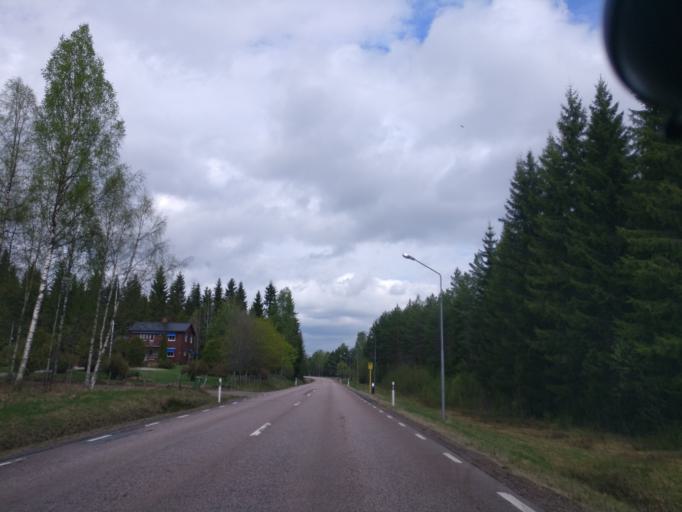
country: SE
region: Vaermland
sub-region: Hagfors Kommun
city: Ekshaerad
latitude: 60.1397
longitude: 13.5252
